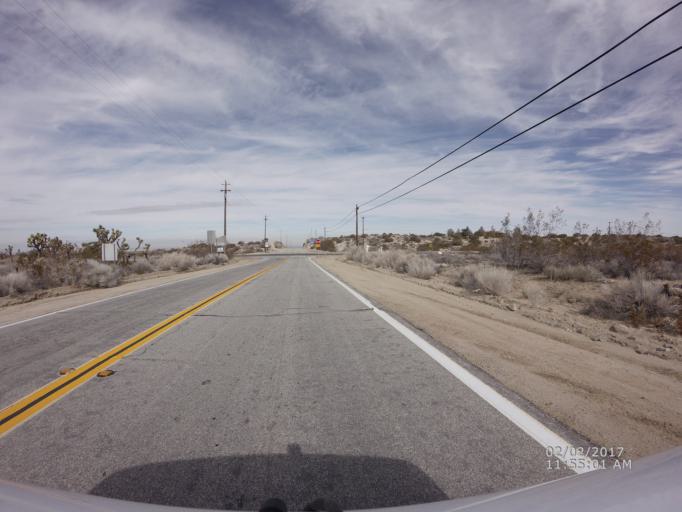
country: US
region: California
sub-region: Los Angeles County
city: Littlerock
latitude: 34.4915
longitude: -117.9401
